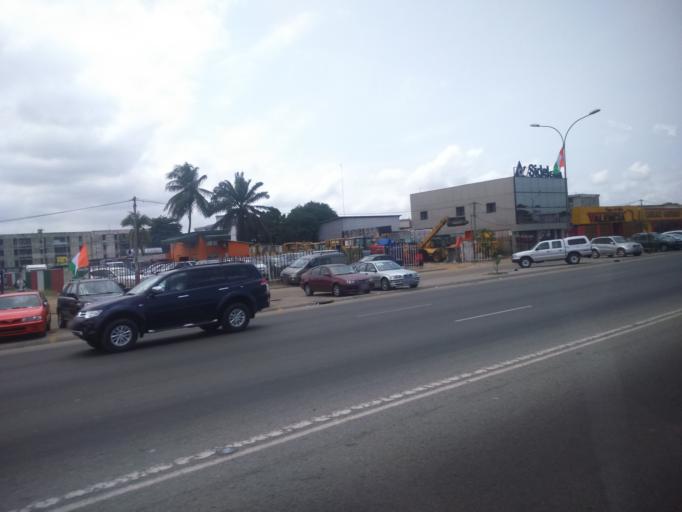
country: CI
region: Lagunes
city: Abidjan
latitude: 5.2937
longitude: -3.9773
